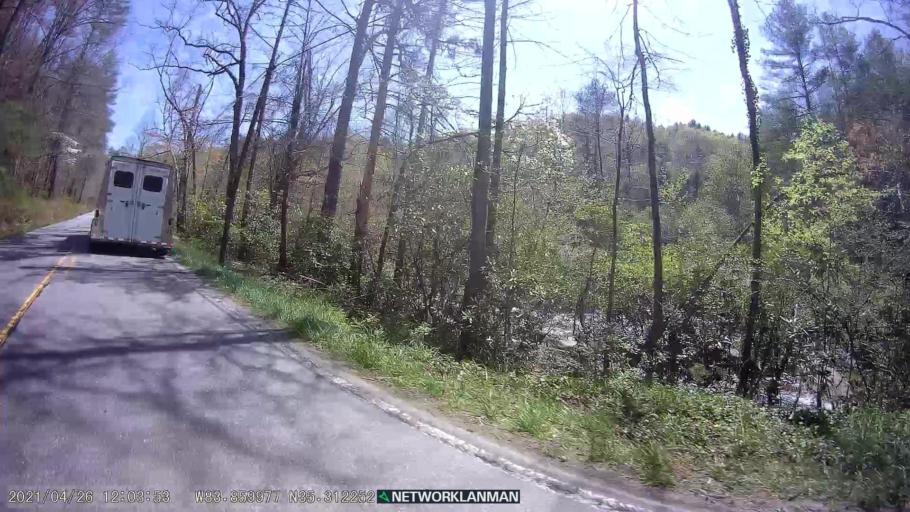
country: US
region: North Carolina
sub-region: Graham County
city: Robbinsville
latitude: 35.3122
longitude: -83.8599
